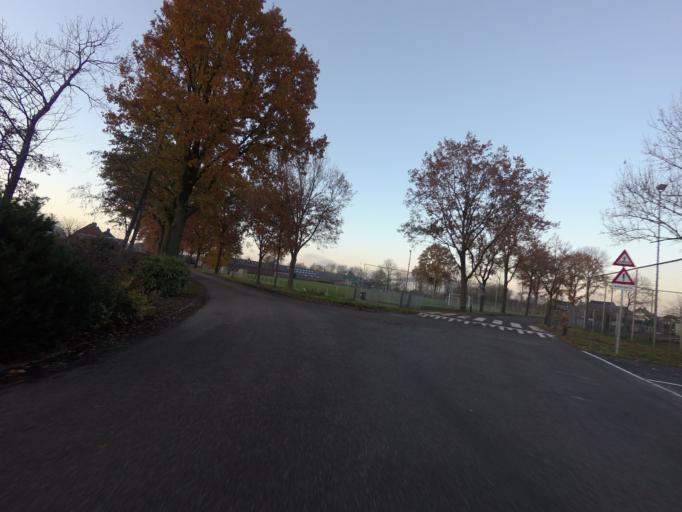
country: NL
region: Gelderland
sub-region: Gemeente Maasdriel
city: Hedel
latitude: 51.7539
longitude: 5.2277
